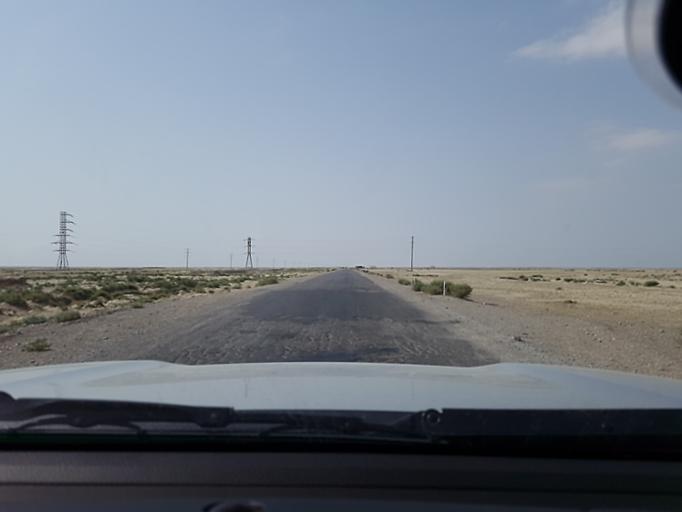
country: TM
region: Balkan
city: Gumdag
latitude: 39.0030
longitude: 54.5860
